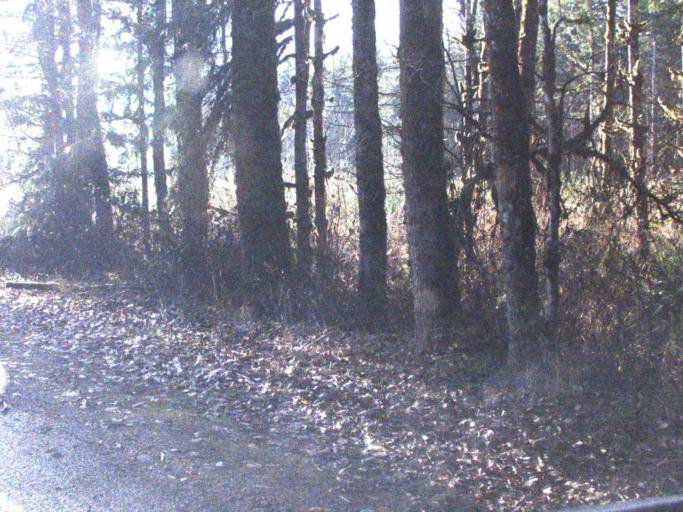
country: US
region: Washington
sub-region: Snohomish County
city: Darrington
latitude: 48.4815
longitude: -121.5921
